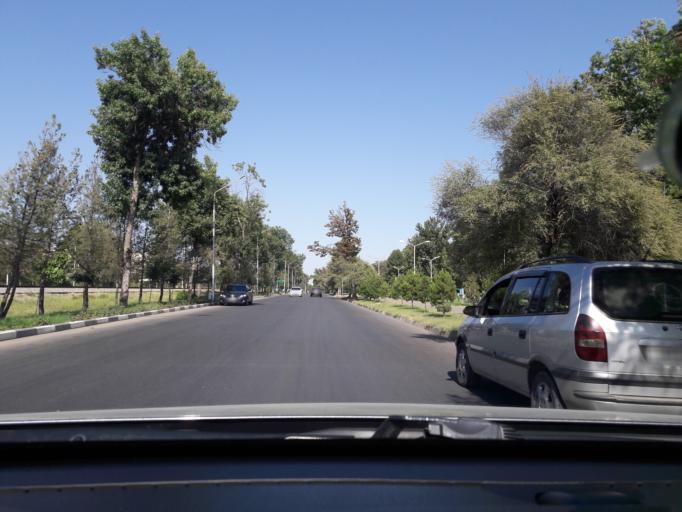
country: TJ
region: Dushanbe
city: Dushanbe
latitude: 38.5680
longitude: 68.7448
